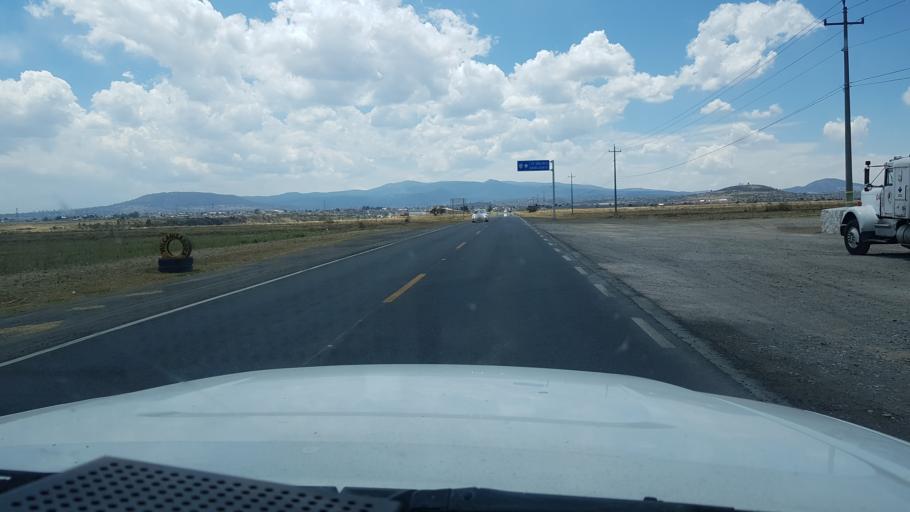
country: MX
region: Hidalgo
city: Calpulalpan
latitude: 19.6121
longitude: -98.5571
